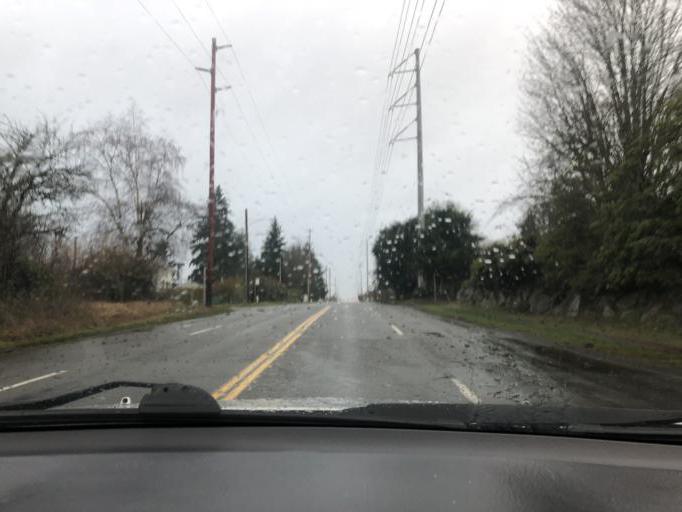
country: US
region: Washington
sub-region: Pierce County
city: Midland
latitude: 47.1918
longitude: -122.4018
